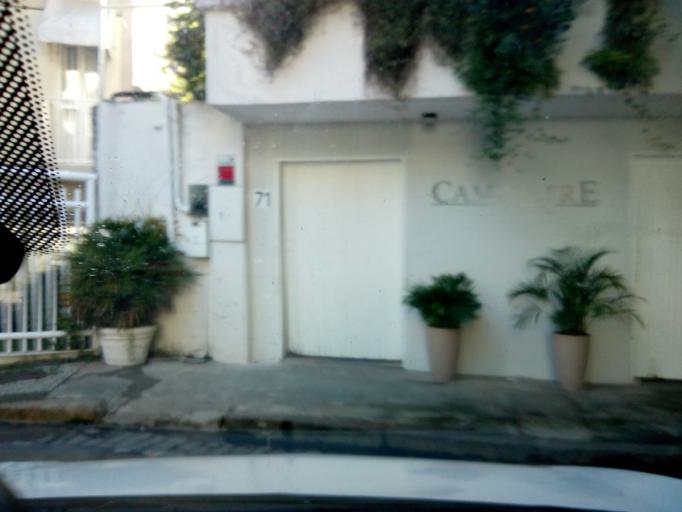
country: BR
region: Rio de Janeiro
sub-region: Rio De Janeiro
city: Rio de Janeiro
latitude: -22.9871
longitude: -43.2325
